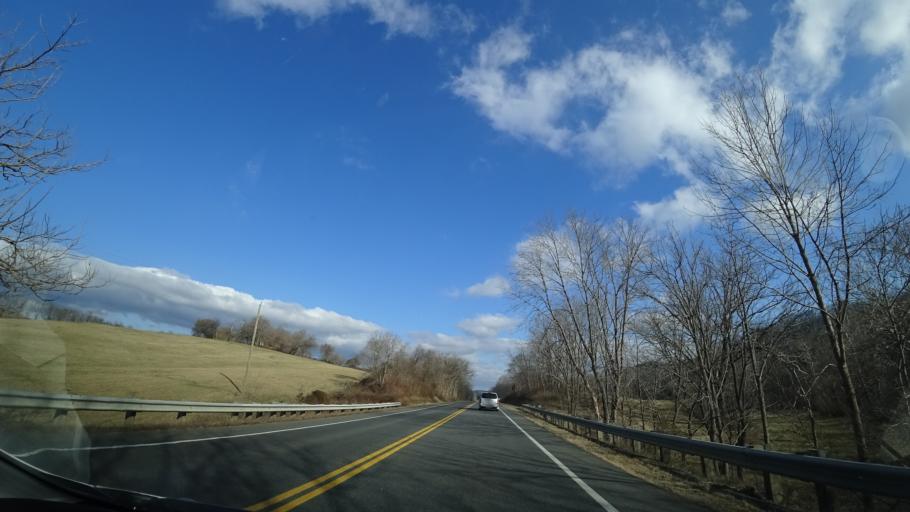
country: US
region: Virginia
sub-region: Fauquier County
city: Marshall
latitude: 38.9306
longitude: -77.9321
